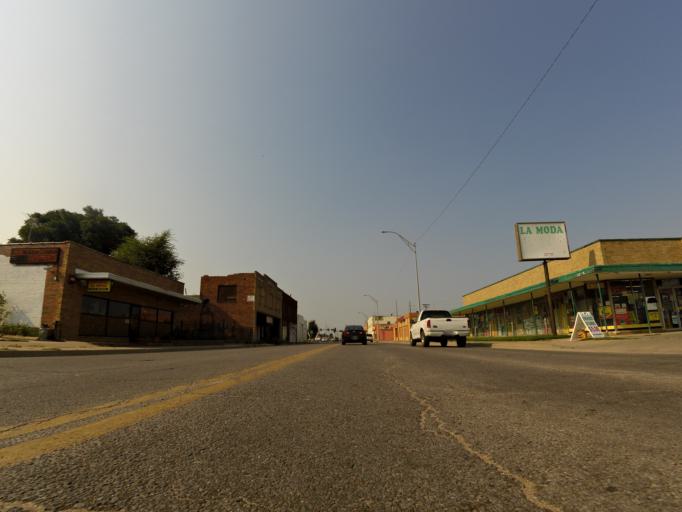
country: US
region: Kansas
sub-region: Sedgwick County
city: Wichita
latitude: 37.7208
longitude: -97.3356
